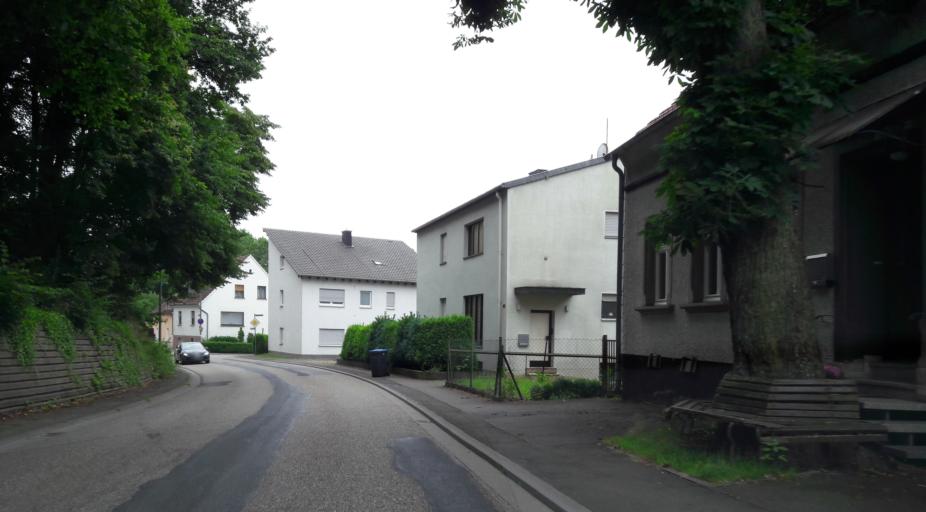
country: DE
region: Rheinland-Pfalz
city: Waldmohr
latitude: 49.3747
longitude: 7.3201
